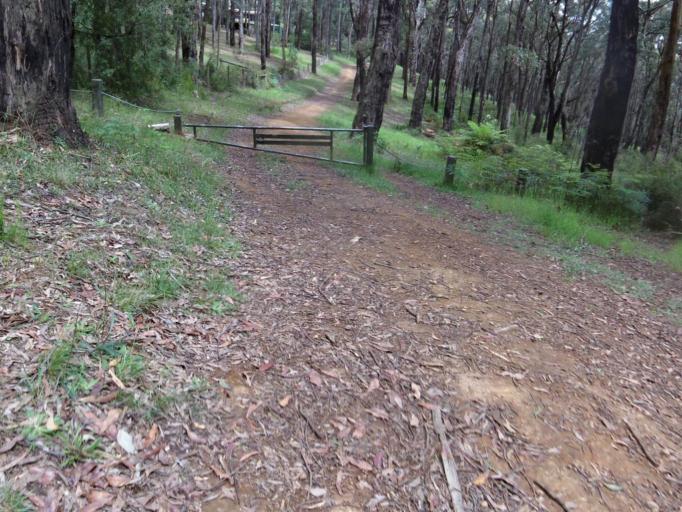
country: AU
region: Victoria
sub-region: Cardinia
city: Cockatoo
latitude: -37.9395
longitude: 145.4750
